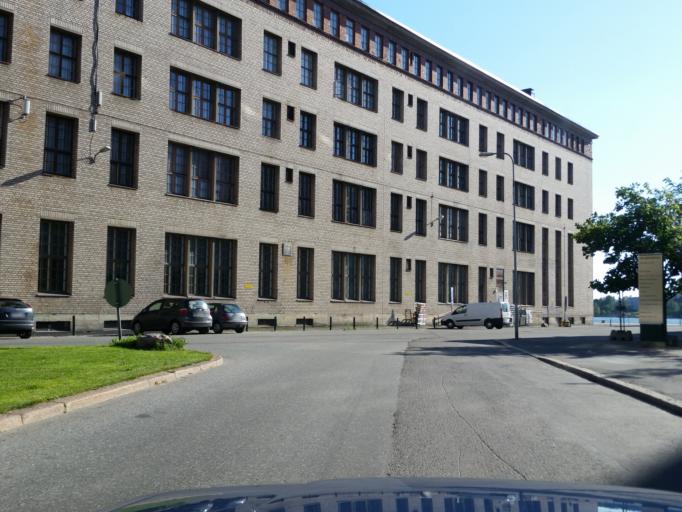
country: FI
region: Uusimaa
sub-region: Helsinki
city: Helsinki
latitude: 60.1625
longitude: 24.9037
